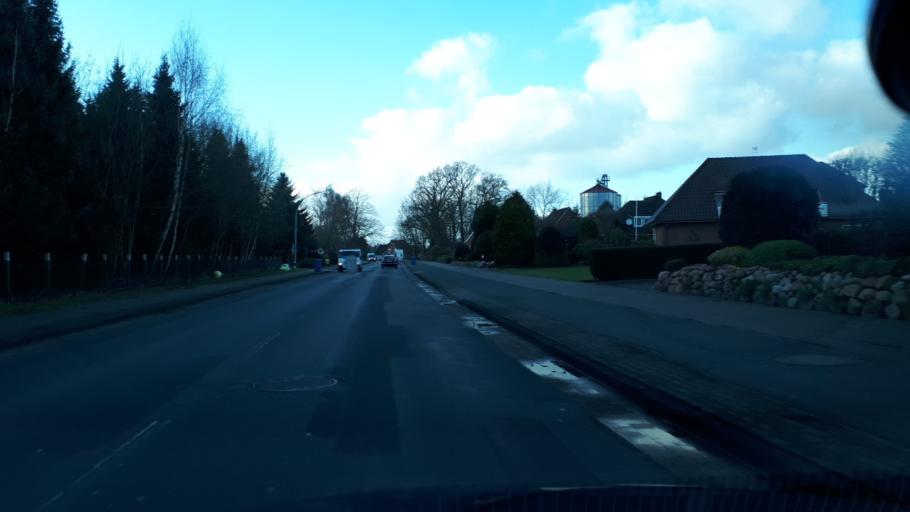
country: DE
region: Lower Saxony
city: Molbergen
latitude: 52.8622
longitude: 7.9130
